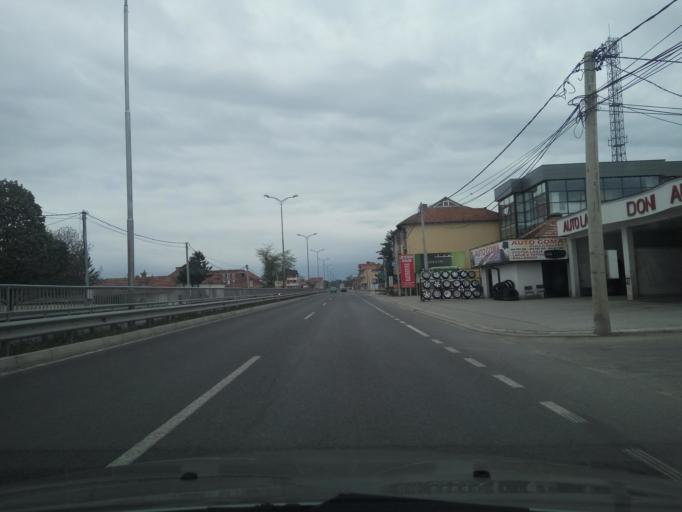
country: XK
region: Pristina
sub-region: Komuna e Obiliqit
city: Obiliq
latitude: 42.7216
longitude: 21.0864
